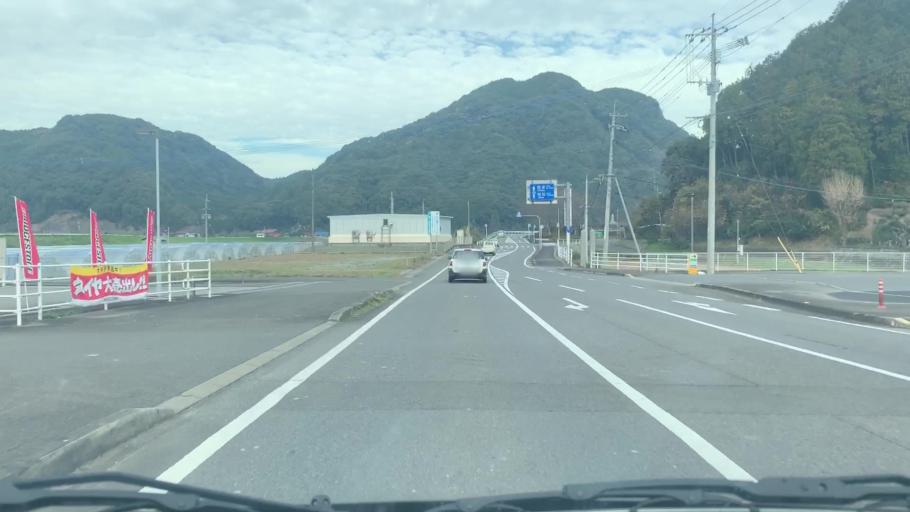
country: JP
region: Saga Prefecture
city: Imaricho-ko
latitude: 33.3018
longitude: 129.9689
